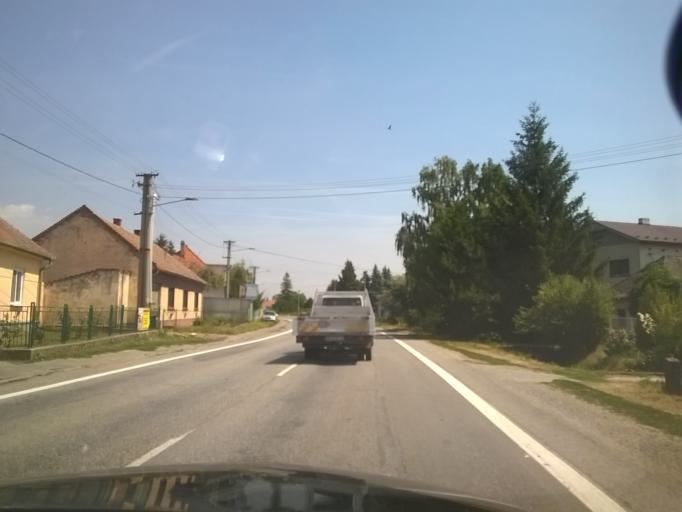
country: SK
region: Nitriansky
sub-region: Okres Nitra
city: Nitra
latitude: 48.4844
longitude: 18.1071
